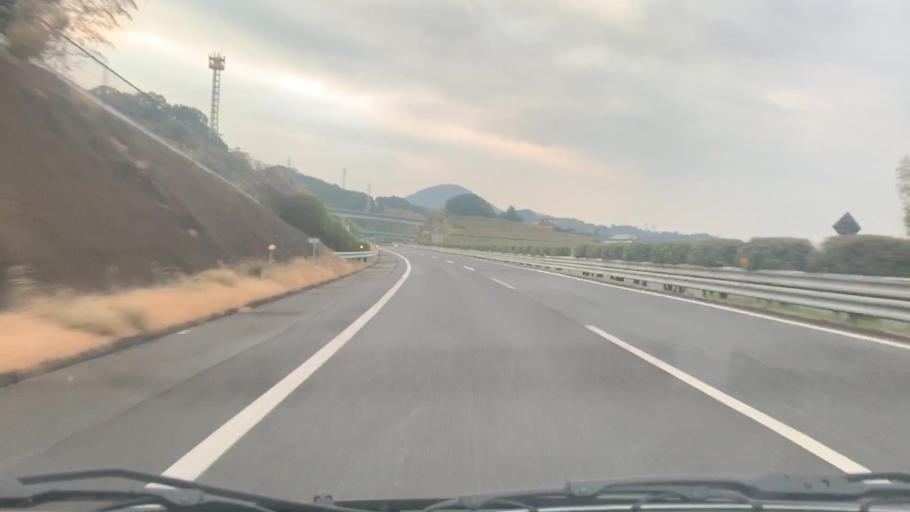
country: JP
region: Nagasaki
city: Omura
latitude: 33.0121
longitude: 129.9512
